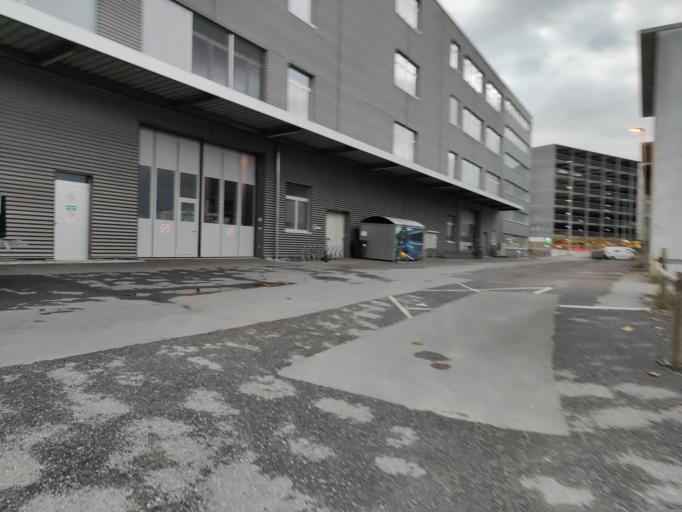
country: LI
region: Eschen
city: Eschen
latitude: 47.2074
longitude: 9.5324
